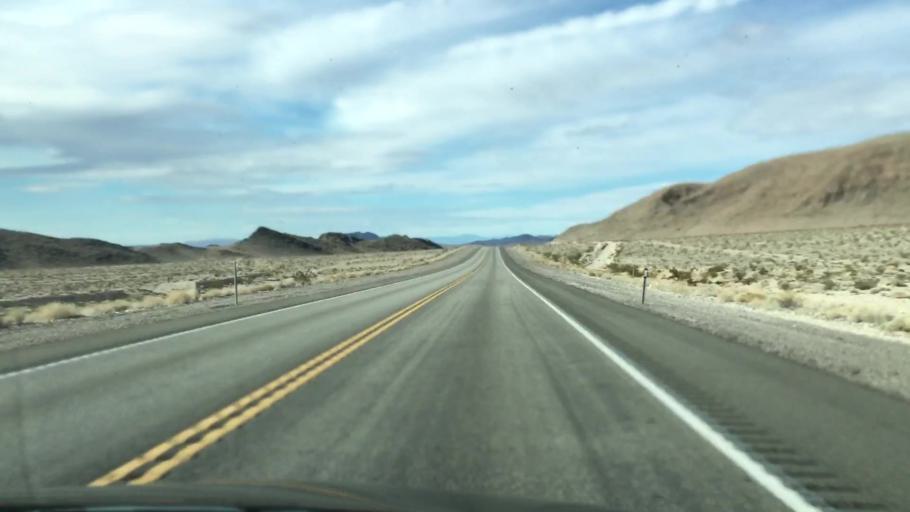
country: US
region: Nevada
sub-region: Nye County
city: Pahrump
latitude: 36.5787
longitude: -116.1974
